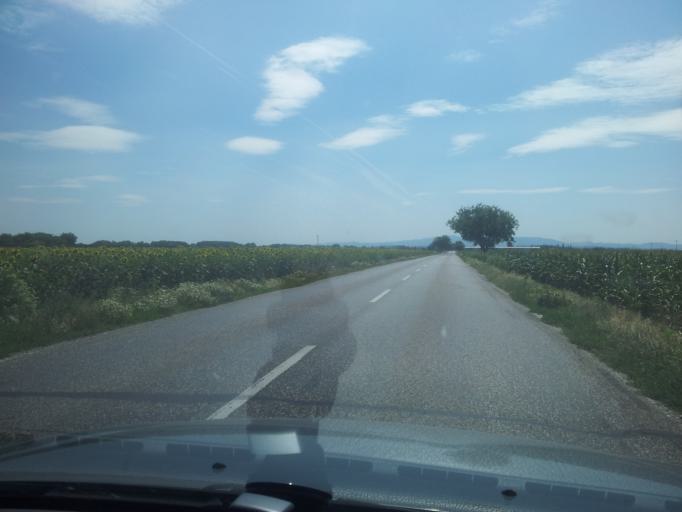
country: SK
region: Nitriansky
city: Zeliezovce
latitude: 48.1197
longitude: 18.6110
